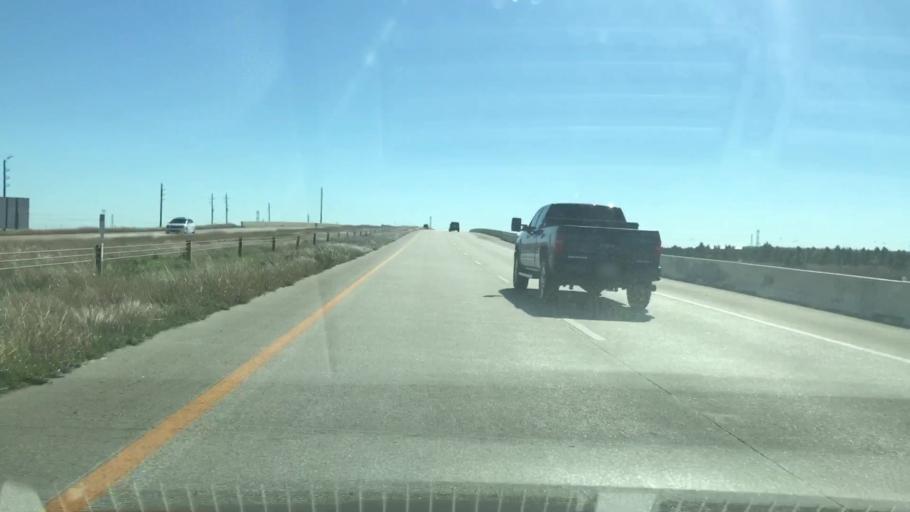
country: US
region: Texas
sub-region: Harris County
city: Cypress
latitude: 29.9249
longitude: -95.7625
